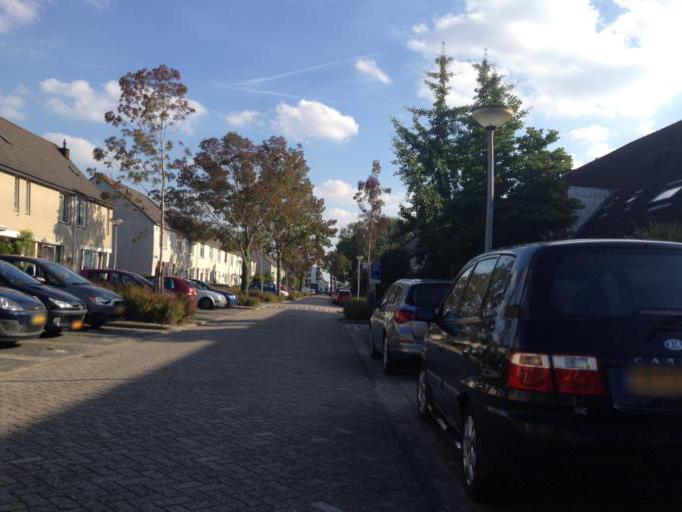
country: NL
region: Flevoland
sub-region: Gemeente Almere
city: Almere Stad
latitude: 52.3989
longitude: 5.2551
